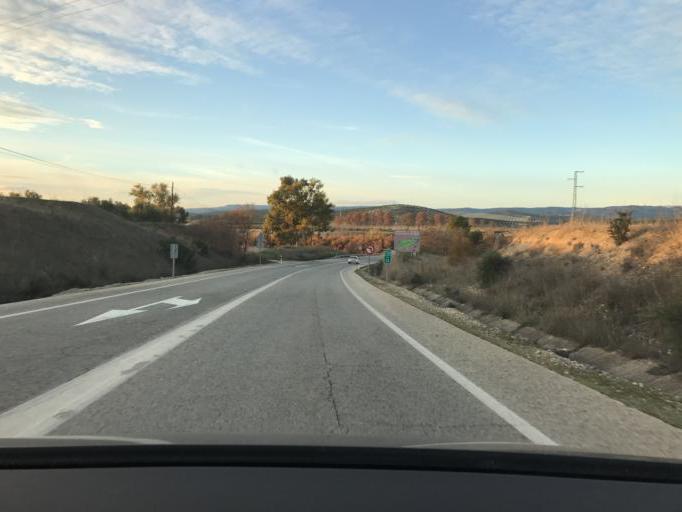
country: ES
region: Andalusia
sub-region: Provincia de Jaen
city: Jodar
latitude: 37.9160
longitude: -3.3485
